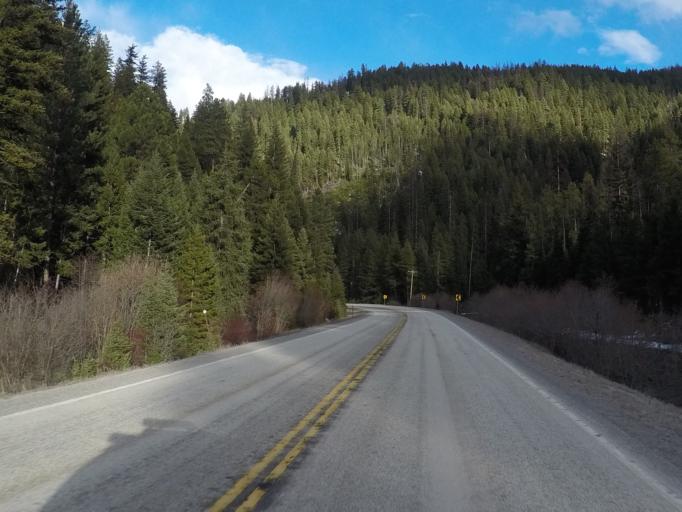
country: US
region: Montana
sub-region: Missoula County
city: Frenchtown
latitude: 46.7594
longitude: -114.4890
